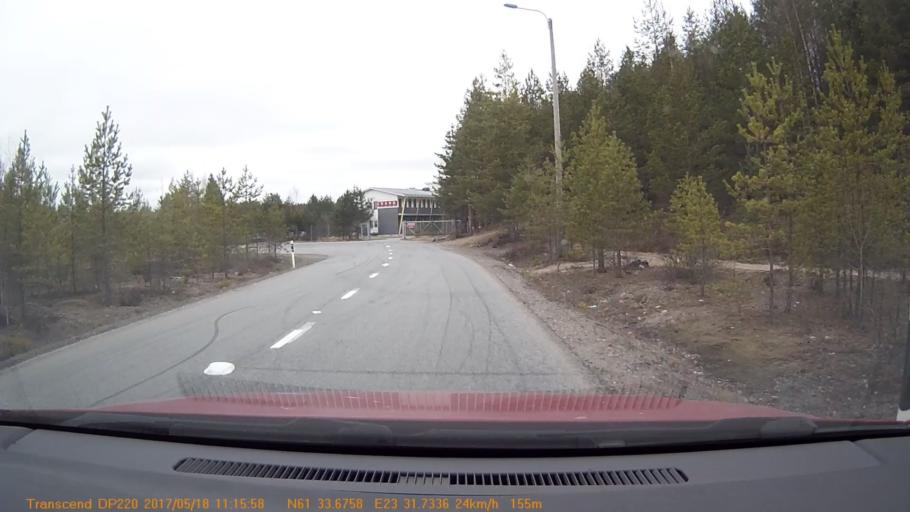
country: FI
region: Pirkanmaa
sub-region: Tampere
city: Yloejaervi
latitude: 61.5613
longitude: 23.5289
